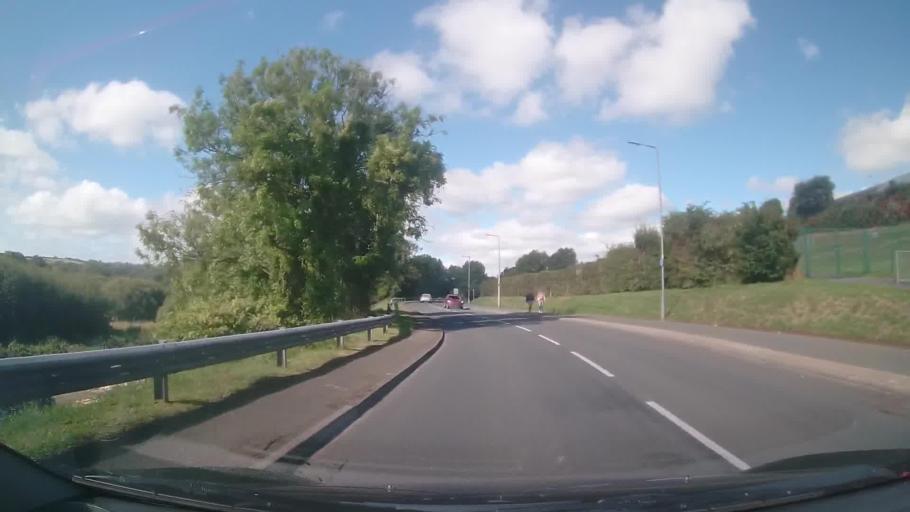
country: GB
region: Wales
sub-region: Pembrokeshire
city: Tenby
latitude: 51.6720
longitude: -4.7128
